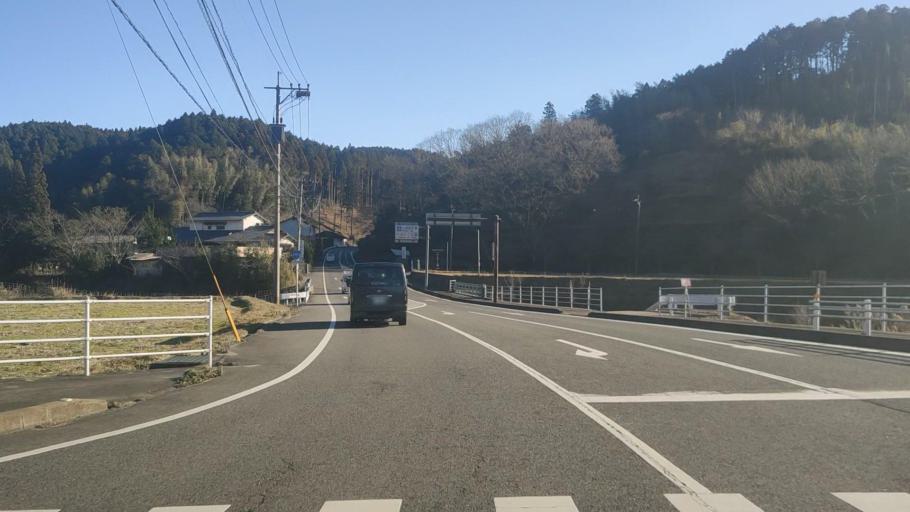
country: JP
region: Saga Prefecture
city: Kanzakimachi-kanzaki
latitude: 33.4222
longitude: 130.2775
